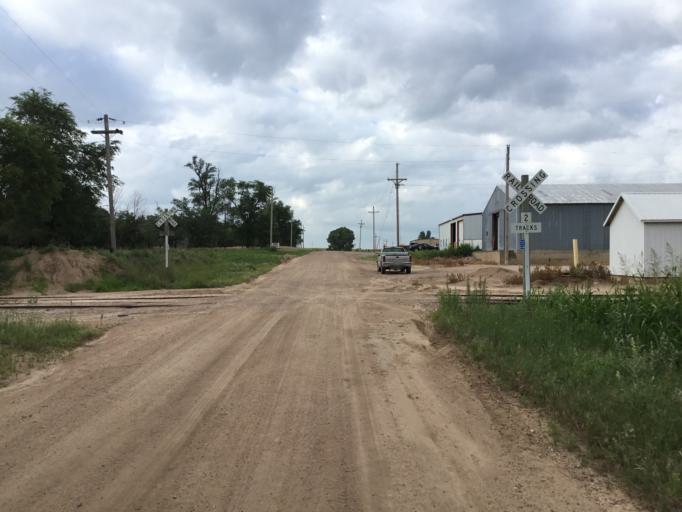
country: US
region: Kansas
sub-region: Pratt County
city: Pratt
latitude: 37.6550
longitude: -98.6098
